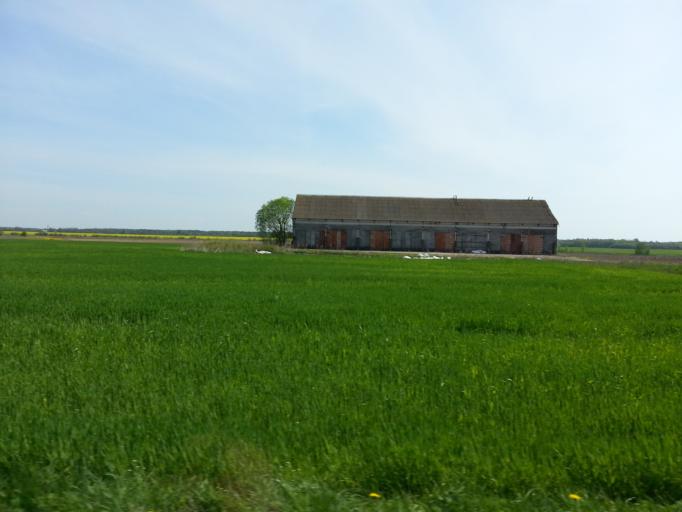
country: LT
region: Panevezys
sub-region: Panevezys City
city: Panevezys
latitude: 55.8489
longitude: 24.2465
